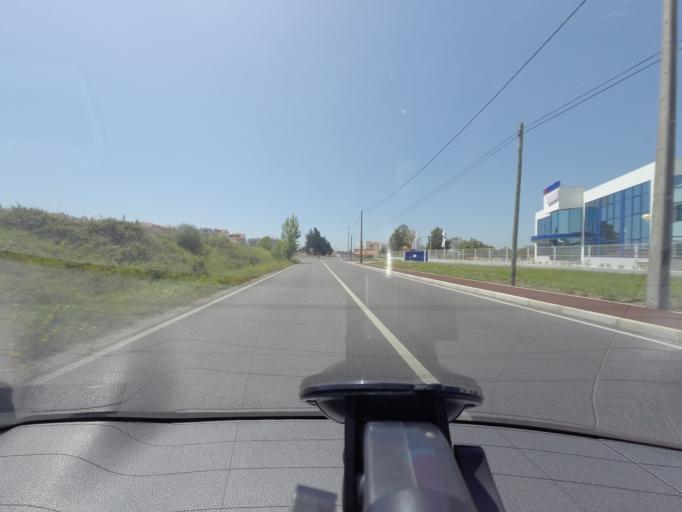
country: PT
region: Lisbon
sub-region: Cascais
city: Parede
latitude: 38.7296
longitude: -9.3605
